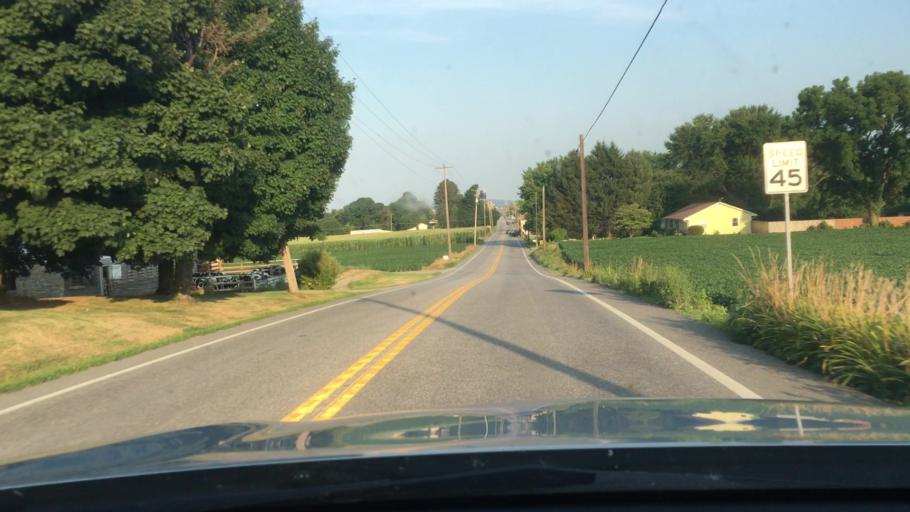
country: US
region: Pennsylvania
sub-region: Cumberland County
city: Boiling Springs
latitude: 40.1641
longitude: -77.1023
